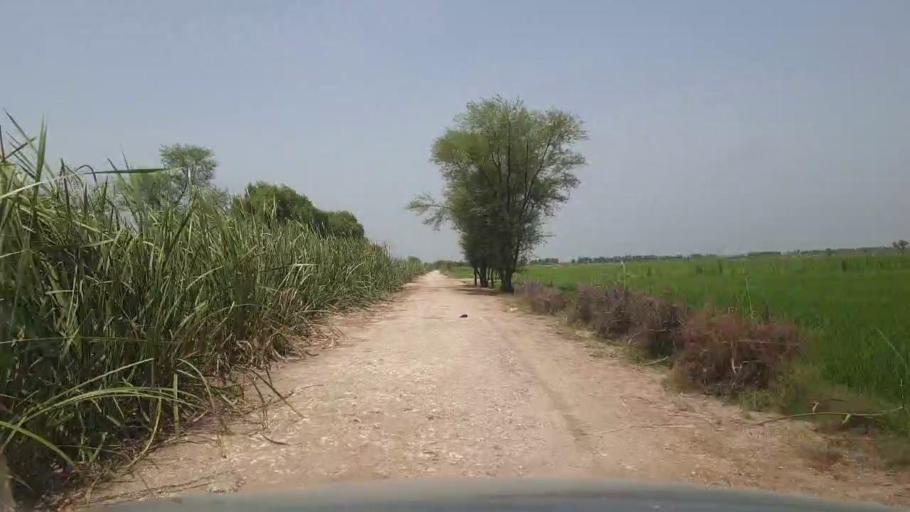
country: PK
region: Sindh
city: Garhi Yasin
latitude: 27.9404
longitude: 68.4306
